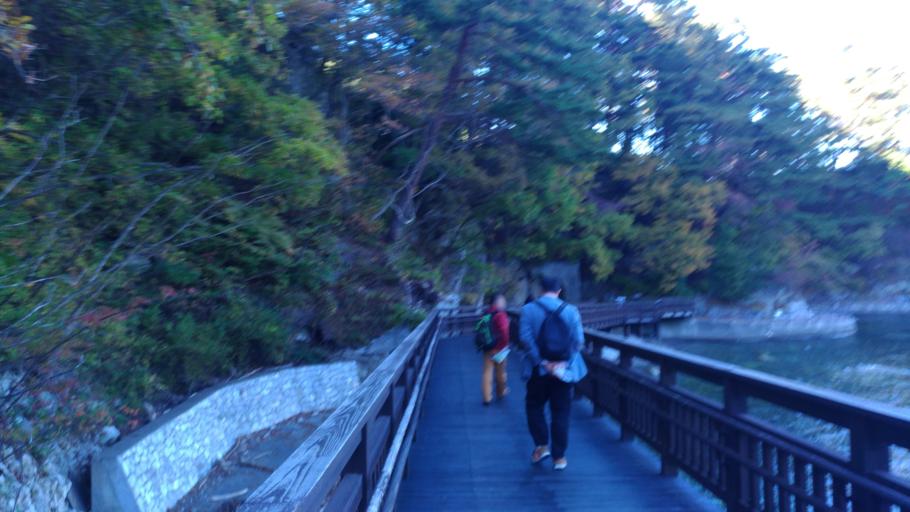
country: JP
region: Iwate
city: Miyako
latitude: 39.6474
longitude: 141.9794
